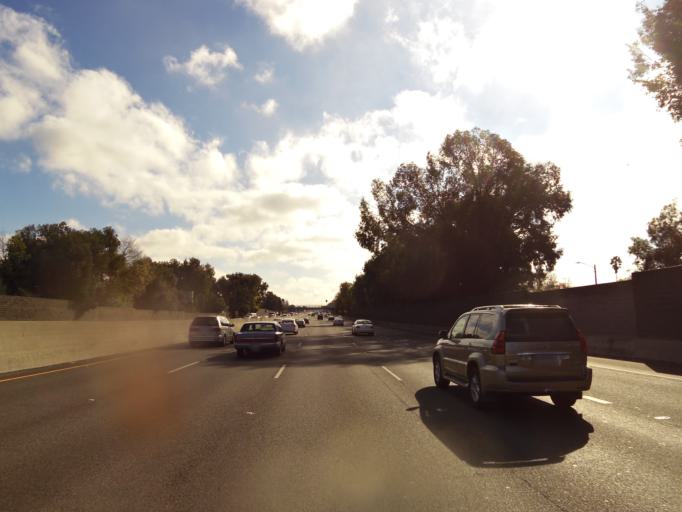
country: US
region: California
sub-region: Sacramento County
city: Parkway
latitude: 38.5320
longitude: -121.4716
